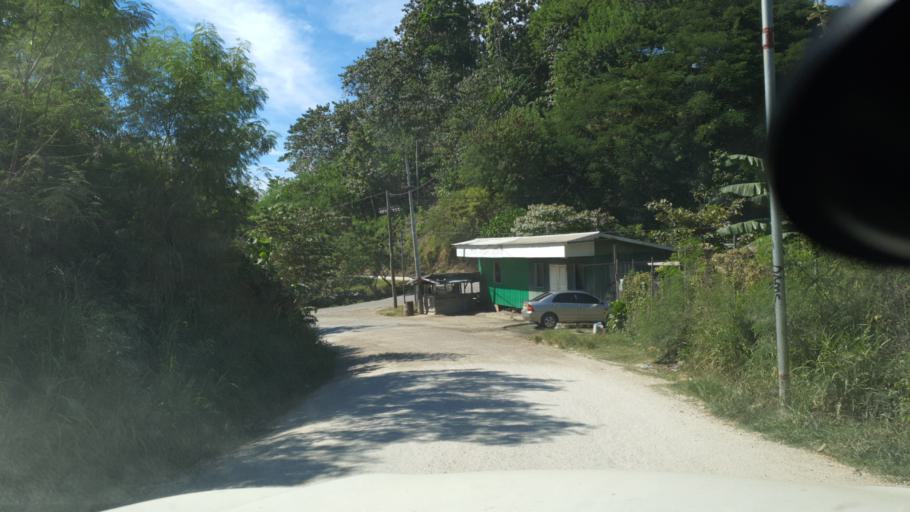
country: SB
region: Guadalcanal
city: Honiara
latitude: -9.4402
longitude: 159.9691
